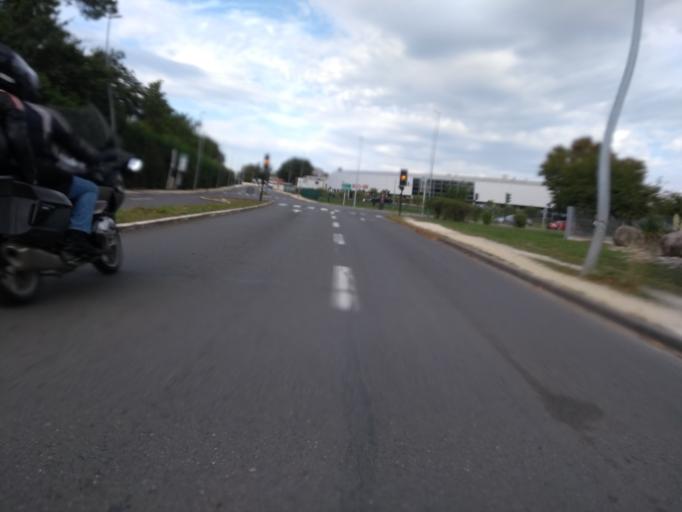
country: FR
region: Aquitaine
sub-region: Departement de la Gironde
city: Pessac
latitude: 44.7890
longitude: -0.6475
